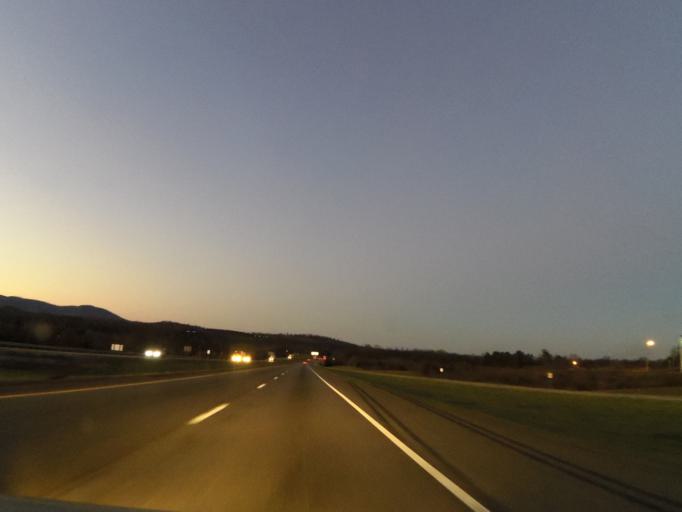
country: US
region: Tennessee
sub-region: Cocke County
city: Newport
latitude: 35.8793
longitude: -83.1867
